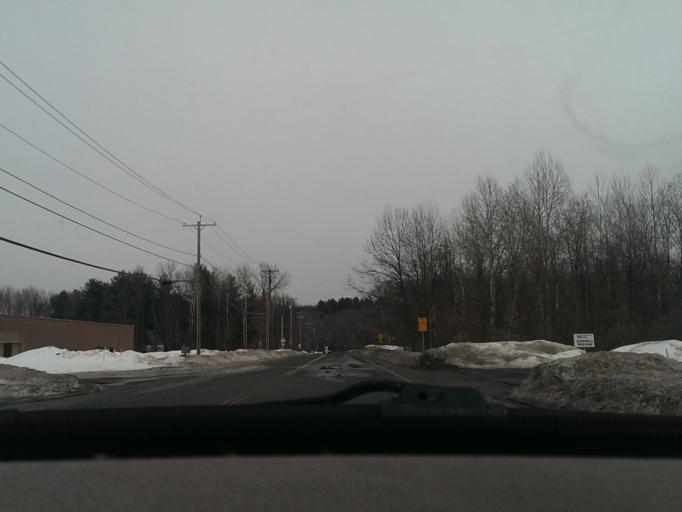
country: US
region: Massachusetts
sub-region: Hampden County
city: East Longmeadow
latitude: 42.0480
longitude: -72.5238
